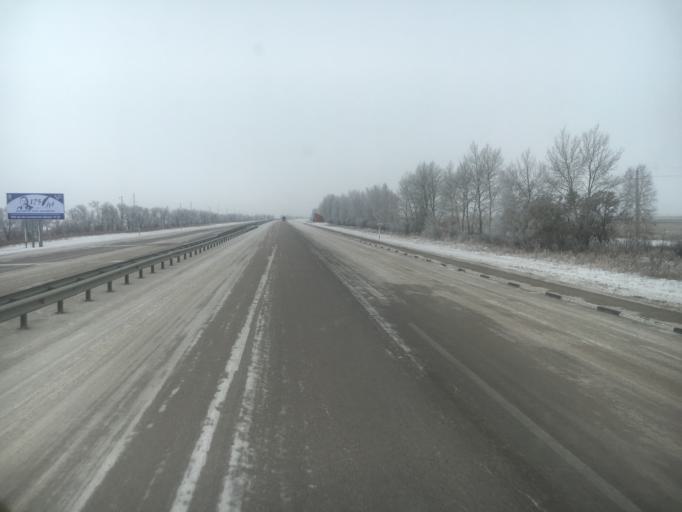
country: KZ
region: Aqmola
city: Akkol'
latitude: 53.3396
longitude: 69.5029
